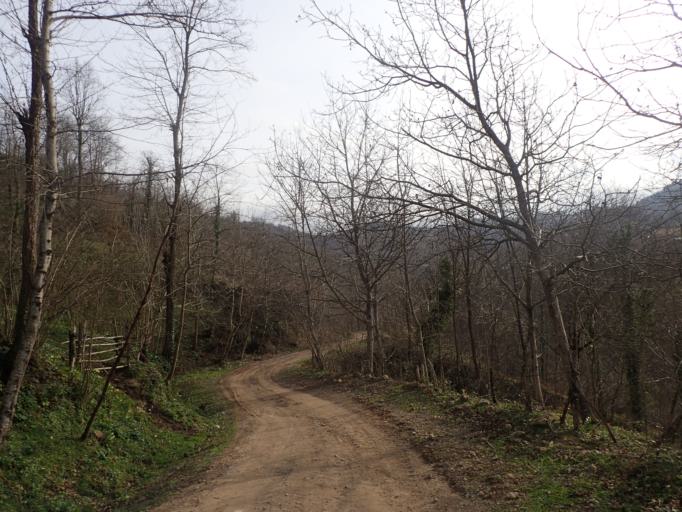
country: TR
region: Ordu
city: Camas
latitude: 40.9303
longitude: 37.5133
